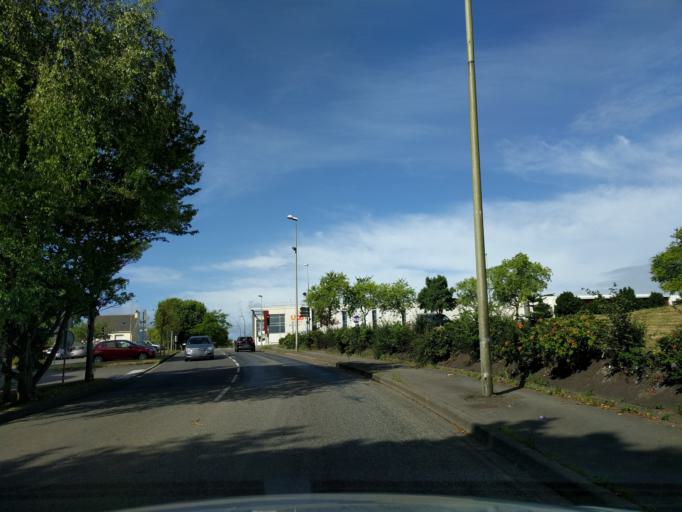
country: FR
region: Brittany
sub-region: Departement du Morbihan
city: Lorient
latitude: 47.7479
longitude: -3.3919
